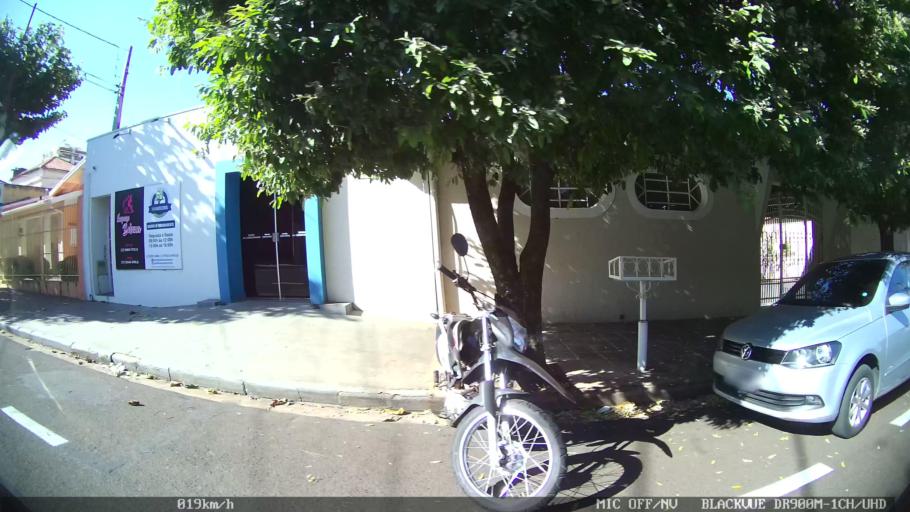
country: BR
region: Sao Paulo
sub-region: Olimpia
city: Olimpia
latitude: -20.7397
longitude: -48.9161
